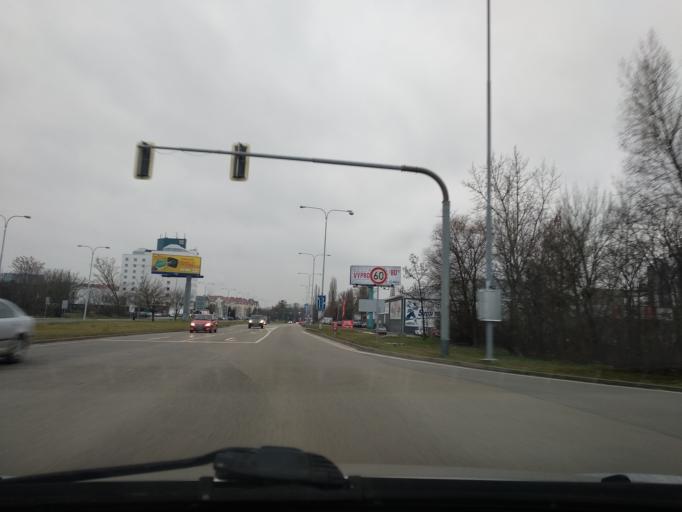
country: CZ
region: South Moravian
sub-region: Mesto Brno
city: Brno
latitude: 49.2141
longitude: 16.6058
